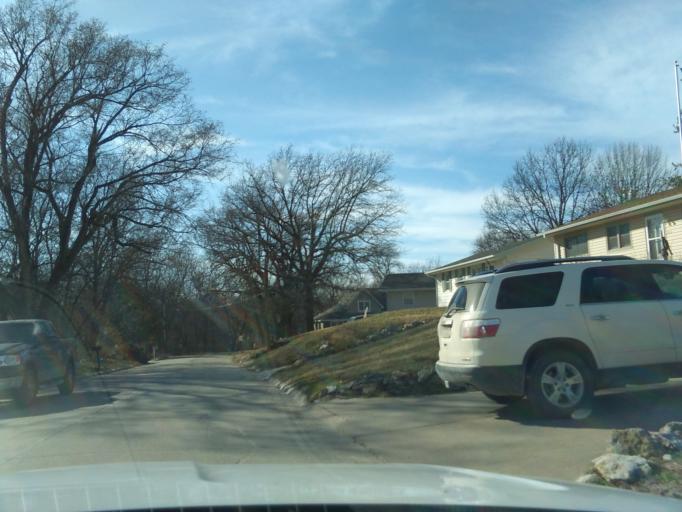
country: US
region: Nebraska
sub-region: Otoe County
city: Nebraska City
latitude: 40.6750
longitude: -95.8716
